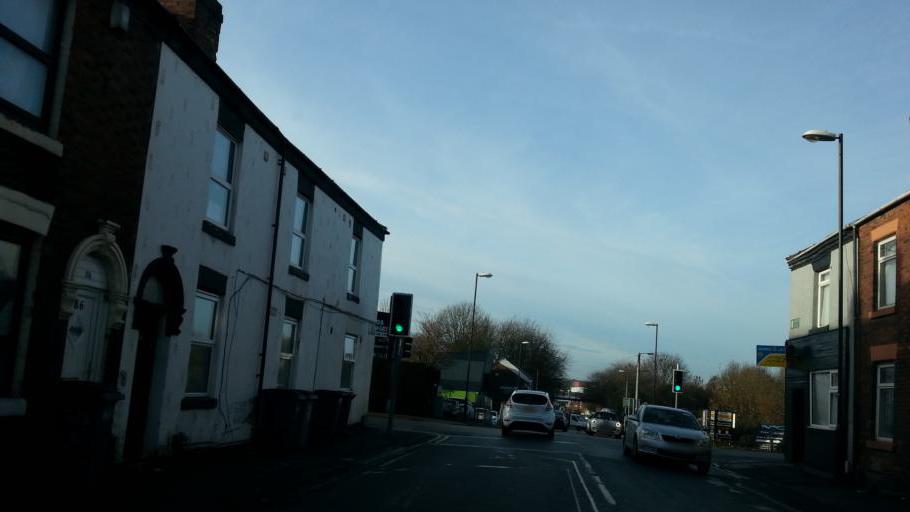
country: GB
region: England
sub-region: Stoke-on-Trent
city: Stoke-on-Trent
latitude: 53.0404
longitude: -2.1835
